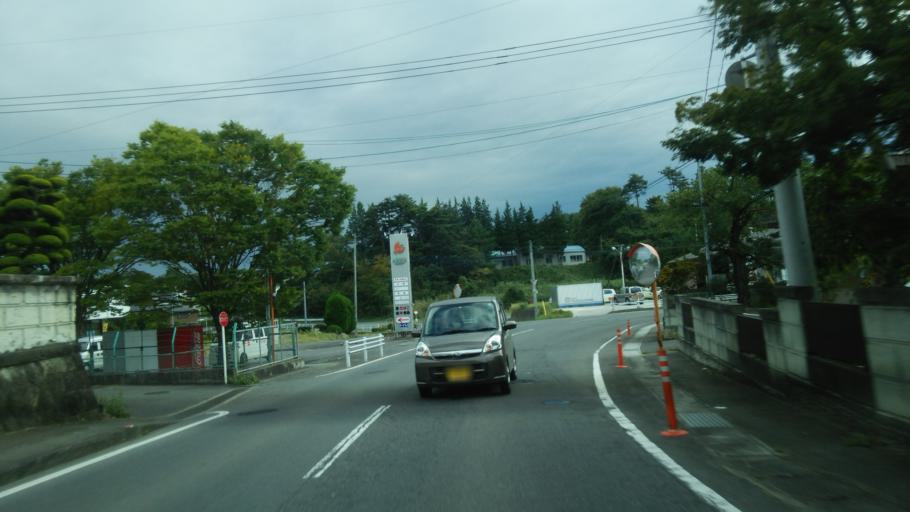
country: JP
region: Fukushima
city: Sukagawa
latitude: 37.3008
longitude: 140.2863
